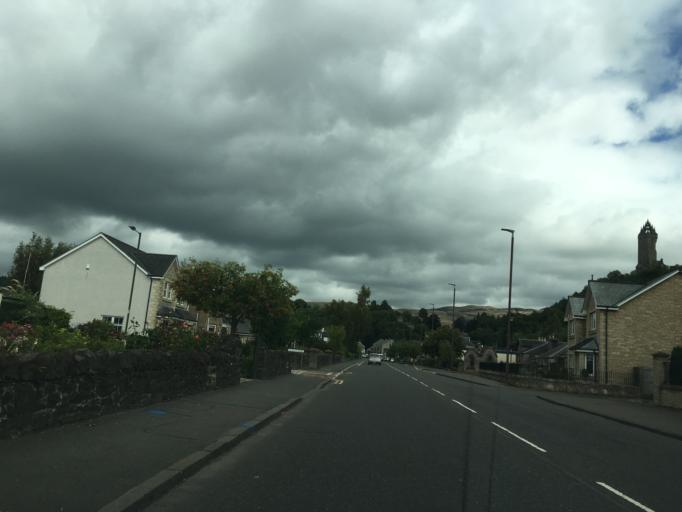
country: GB
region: Scotland
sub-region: Stirling
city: Stirling
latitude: 56.1358
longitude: -3.9269
